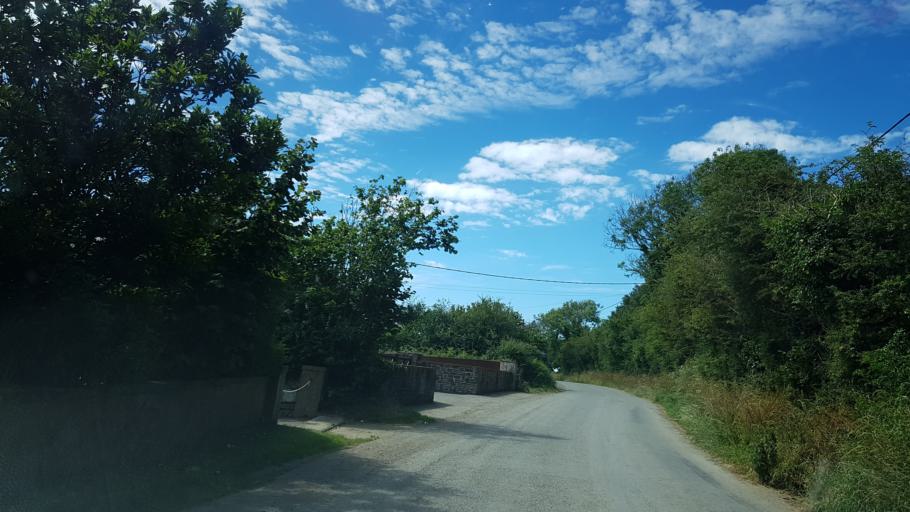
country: GB
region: Wales
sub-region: Pembrokeshire
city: Wiston
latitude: 51.8266
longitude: -4.8752
